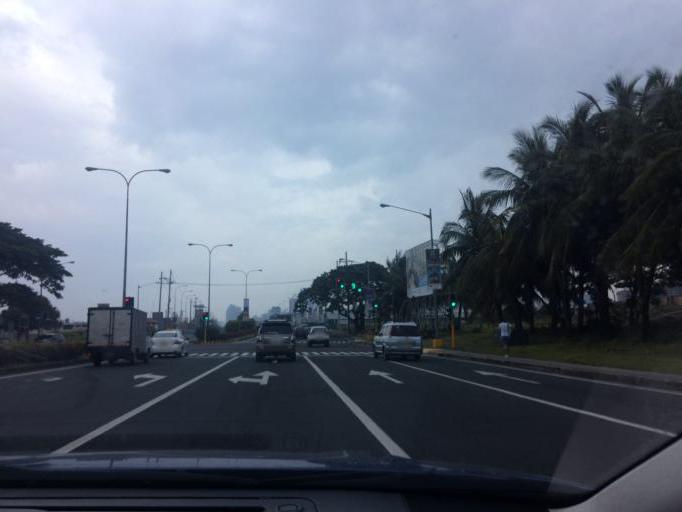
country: PH
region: Metro Manila
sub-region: Makati City
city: Makati City
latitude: 14.5425
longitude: 120.9881
